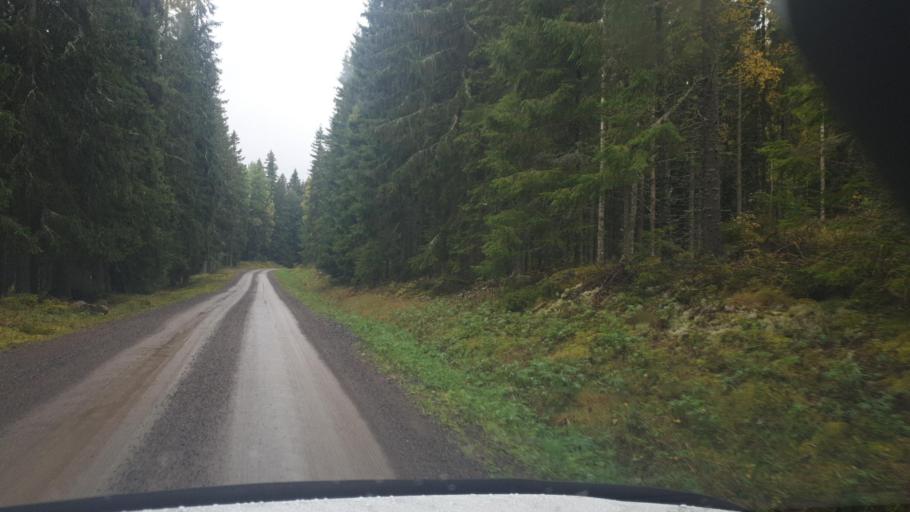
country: SE
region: Vaermland
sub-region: Sunne Kommun
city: Sunne
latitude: 59.8552
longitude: 12.8565
